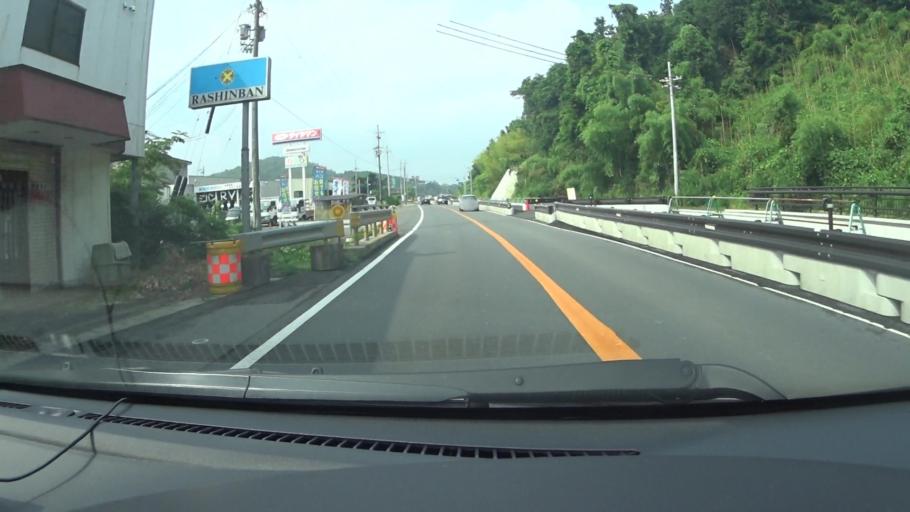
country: JP
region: Kyoto
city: Ayabe
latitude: 35.3057
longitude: 135.2747
